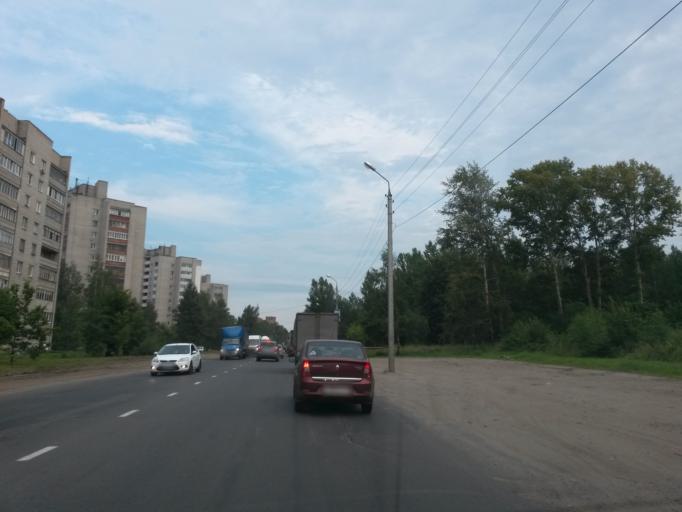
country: RU
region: Jaroslavl
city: Yaroslavl
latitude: 57.5818
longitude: 39.8288
